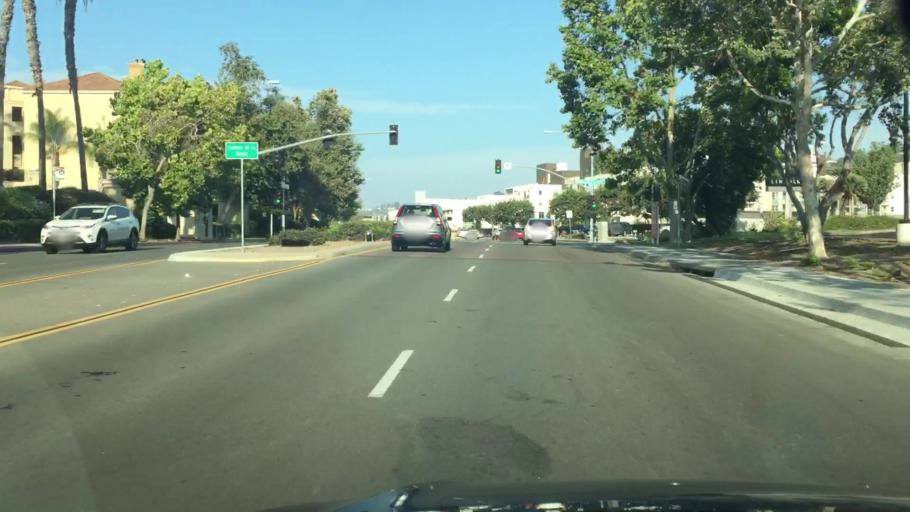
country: US
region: California
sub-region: San Diego County
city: San Diego
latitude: 32.7664
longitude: -117.1615
